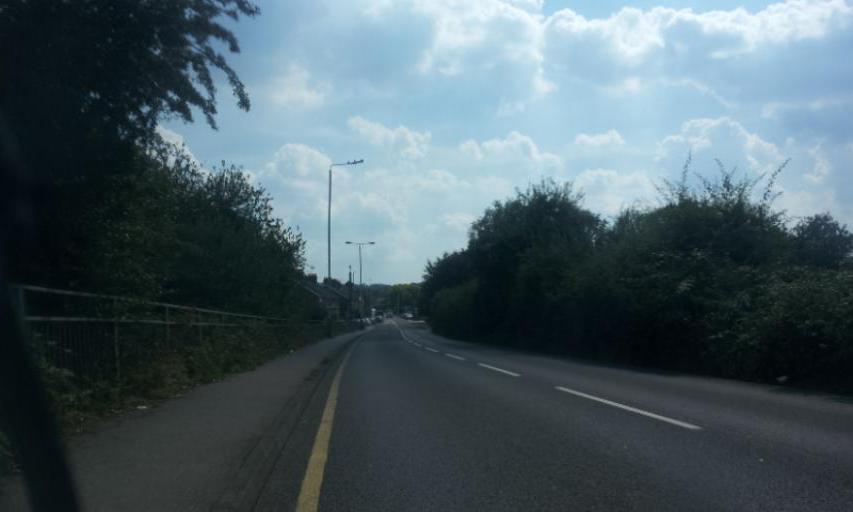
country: GB
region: England
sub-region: Kent
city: Paddock Wood
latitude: 51.1818
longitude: 0.3867
